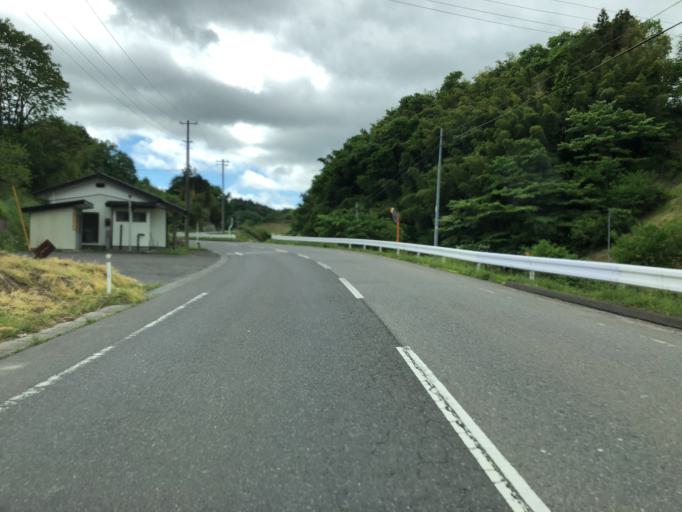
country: JP
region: Fukushima
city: Nihommatsu
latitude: 37.5328
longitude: 140.4578
